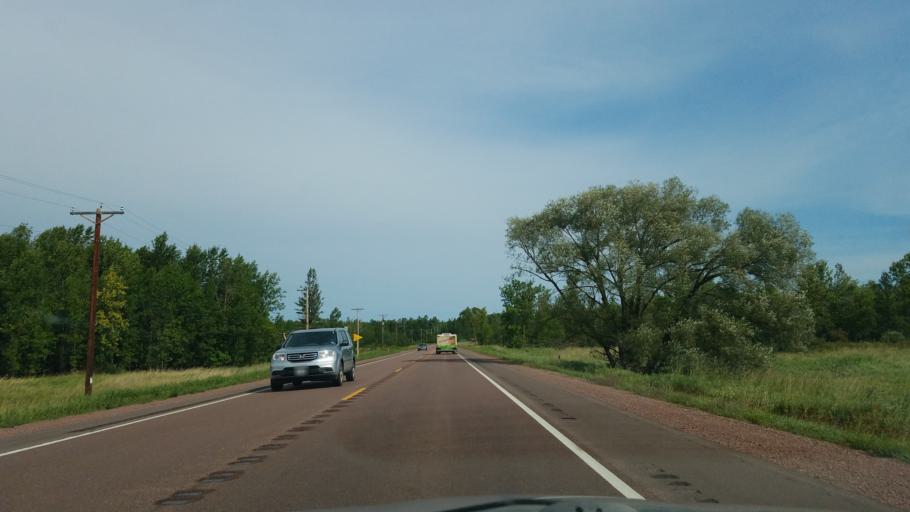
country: US
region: Wisconsin
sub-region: Ashland County
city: Ashland
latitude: 46.5965
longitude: -90.9551
